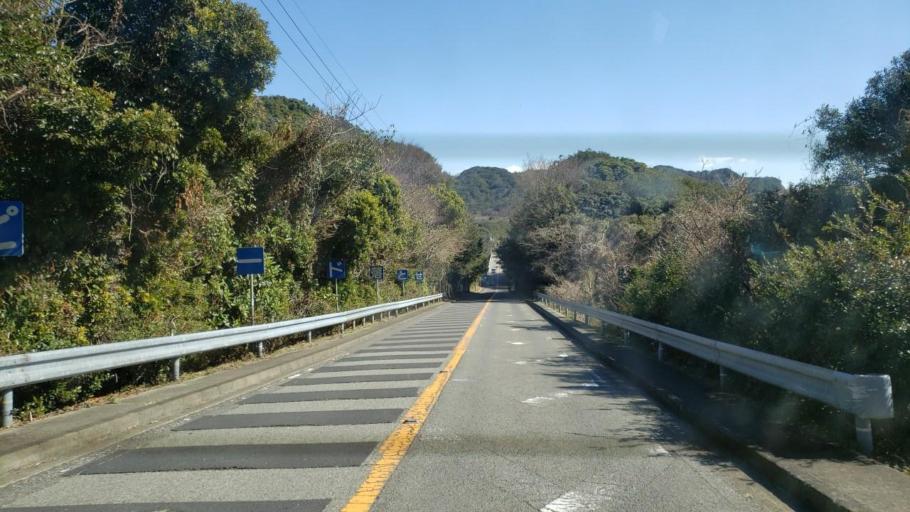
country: JP
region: Tokushima
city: Narutocho-mitsuishi
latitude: 34.2316
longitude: 134.5925
